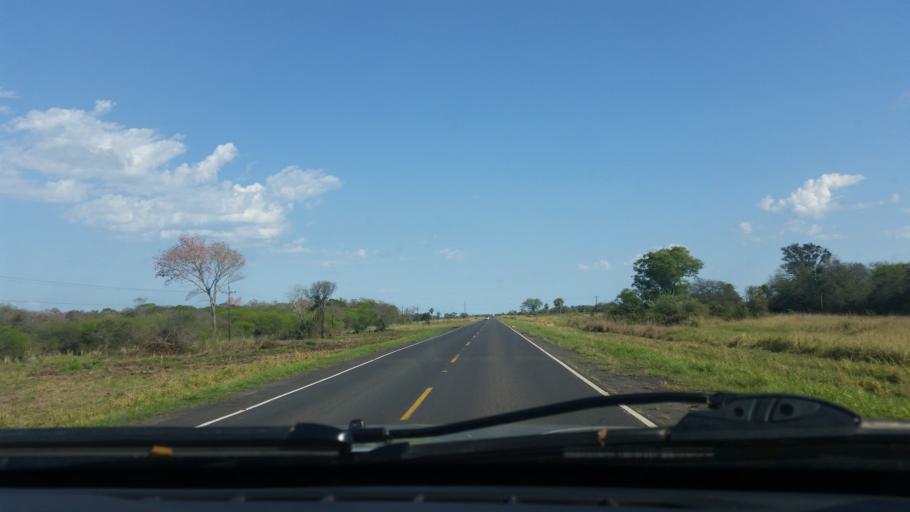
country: PY
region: Presidente Hayes
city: Benjamin Aceval
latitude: -24.8984
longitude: -57.6595
